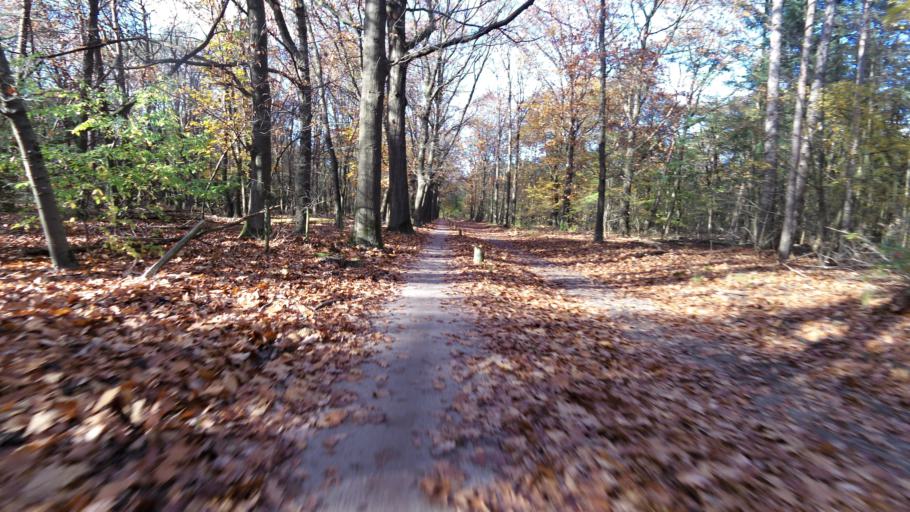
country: NL
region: Gelderland
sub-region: Gemeente Nunspeet
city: Nunspeet
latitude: 52.3536
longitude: 5.8084
